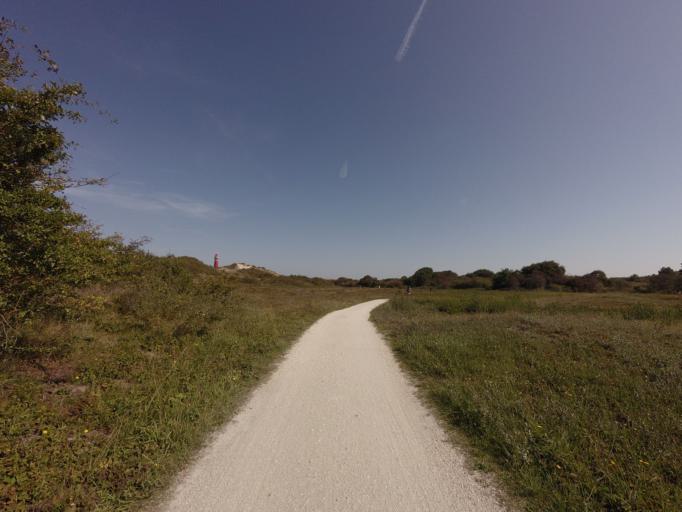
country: NL
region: Friesland
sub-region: Gemeente Schiermonnikoog
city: Schiermonnikoog
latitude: 53.4830
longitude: 6.1461
